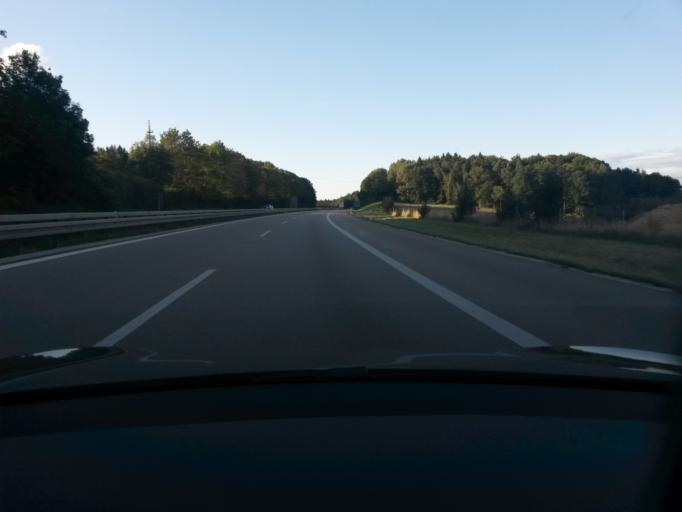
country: DE
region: Bavaria
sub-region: Upper Palatinate
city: Brunn
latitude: 49.0922
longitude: 11.8867
